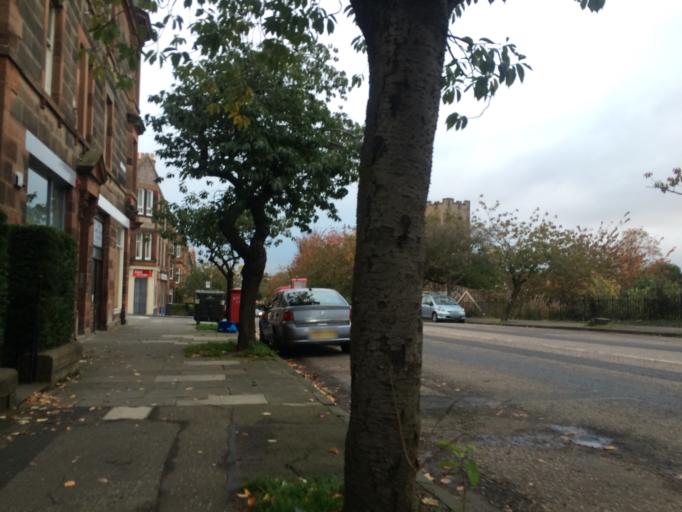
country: GB
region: Scotland
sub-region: Edinburgh
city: Edinburgh
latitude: 55.9258
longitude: -3.1830
